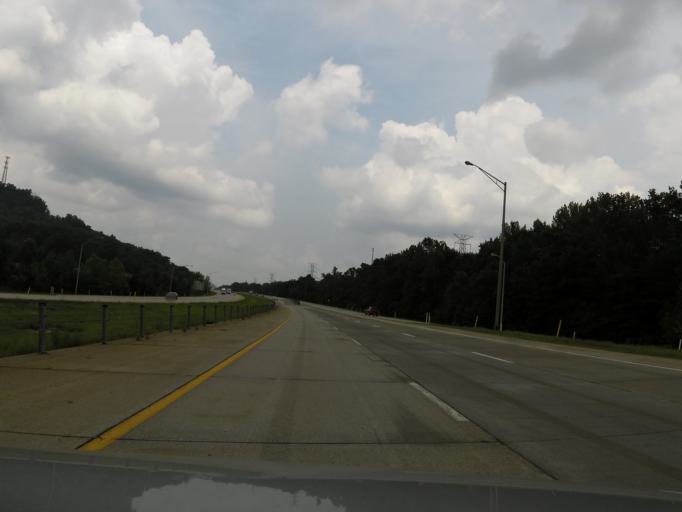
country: US
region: Kentucky
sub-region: Bullitt County
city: Lebanon Junction
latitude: 37.8304
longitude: -85.7189
